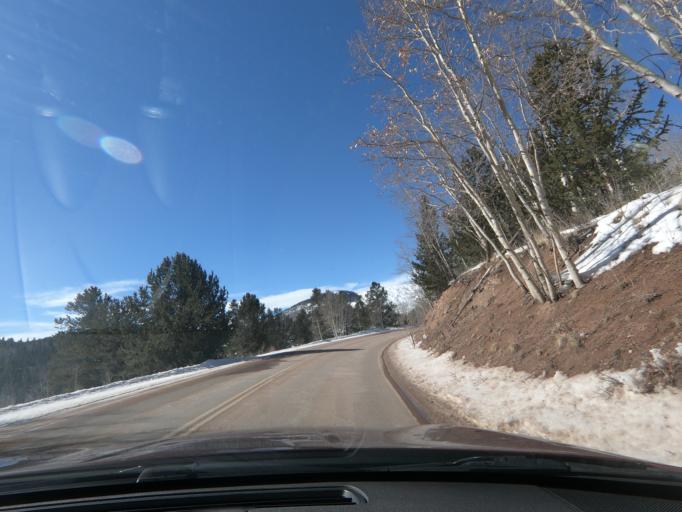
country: US
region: Colorado
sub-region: Teller County
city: Cripple Creek
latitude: 38.7430
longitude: -105.1031
